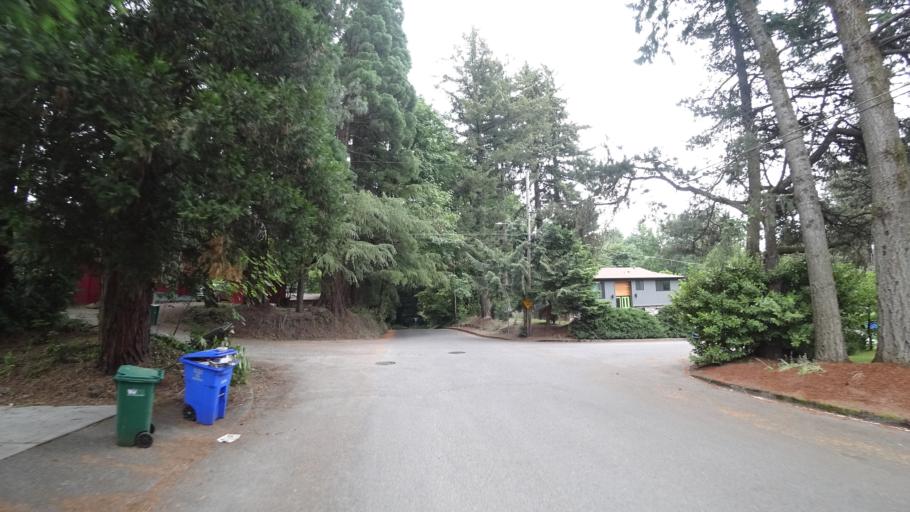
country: US
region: Oregon
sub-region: Clackamas County
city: Lake Oswego
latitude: 45.4556
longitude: -122.6759
